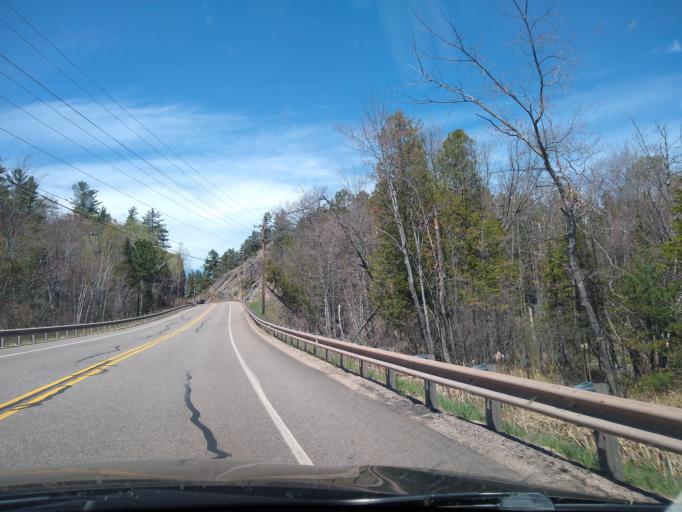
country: US
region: Michigan
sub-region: Marquette County
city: Trowbridge Park
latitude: 46.6034
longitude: -87.4608
